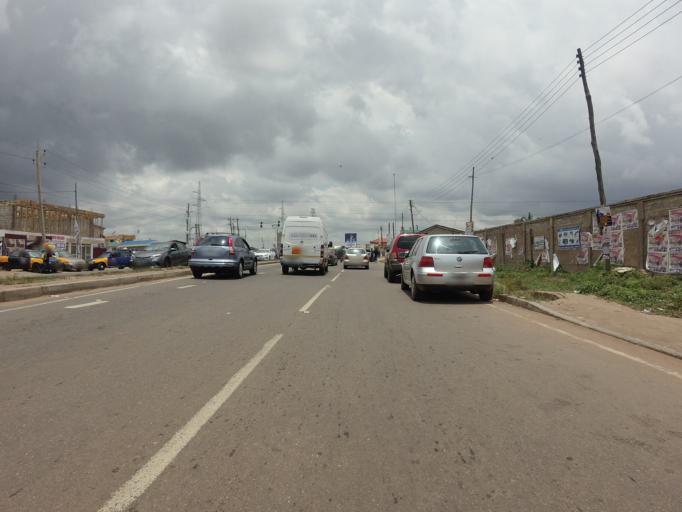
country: GH
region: Greater Accra
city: Medina Estates
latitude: 5.6475
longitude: -0.1499
